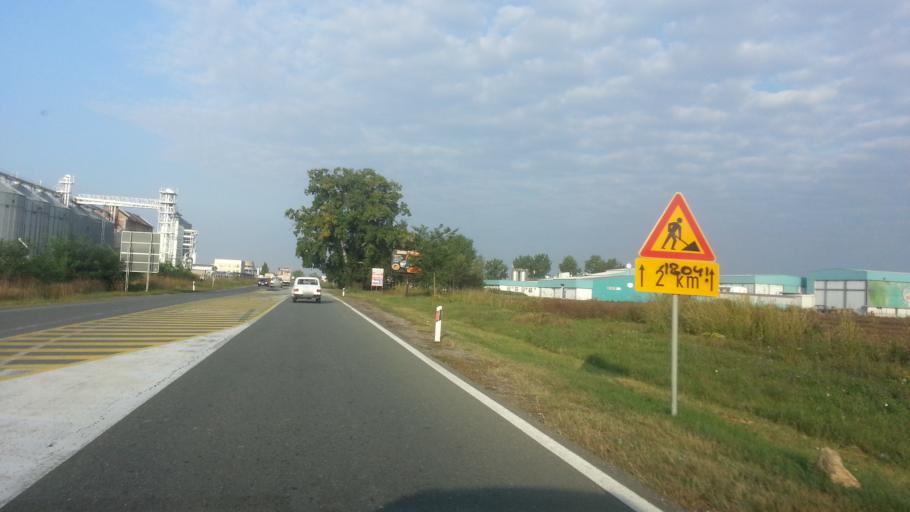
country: RS
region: Autonomna Pokrajina Vojvodina
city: Nova Pazova
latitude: 44.9867
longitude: 20.2086
